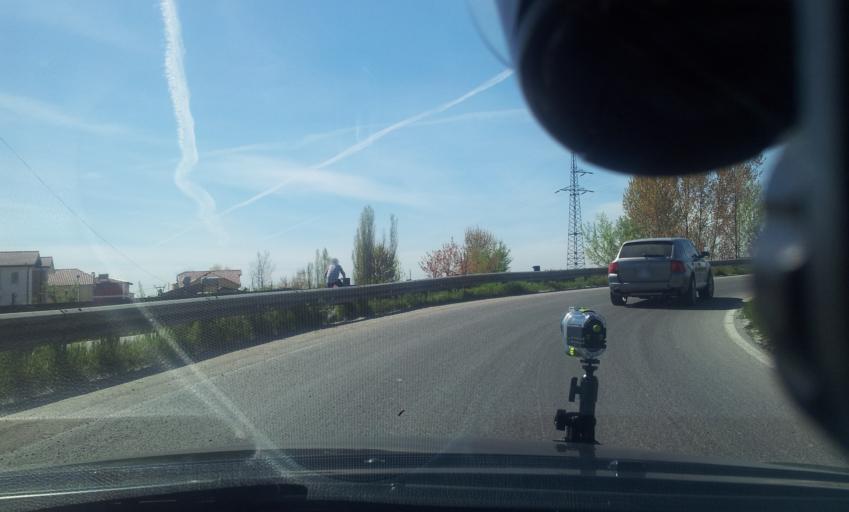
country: AL
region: Durres
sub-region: Rrethi i Krujes
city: Fushe-Kruje
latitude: 41.4776
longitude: 19.7145
